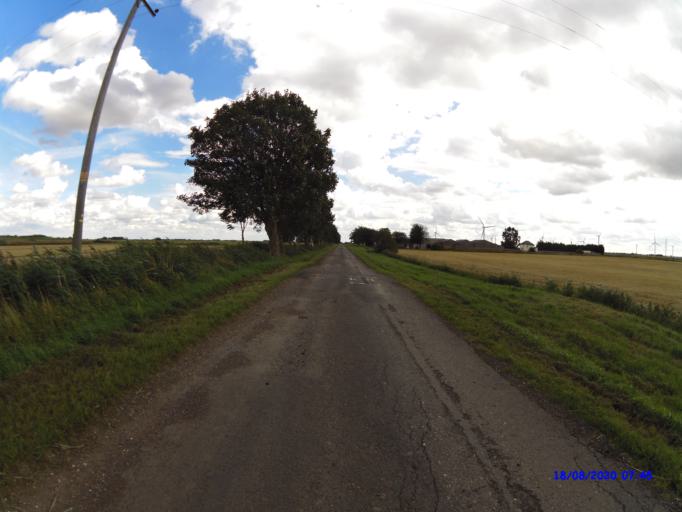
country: GB
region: England
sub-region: Cambridgeshire
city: Whittlesey
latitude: 52.5261
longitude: -0.1023
